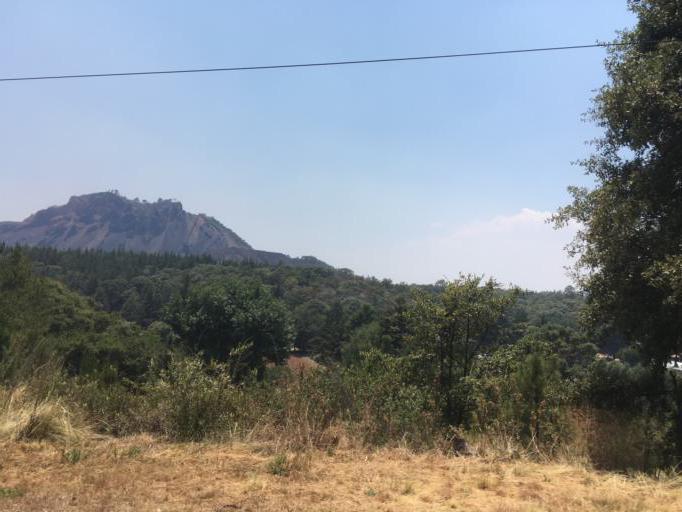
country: MX
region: Michoacan
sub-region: Morelia
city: Iratzio
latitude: 19.6225
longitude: -101.4601
